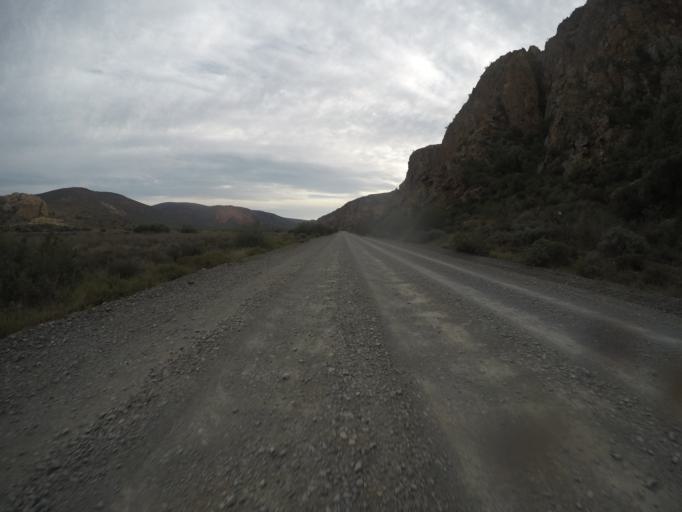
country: ZA
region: Eastern Cape
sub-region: Cacadu District Municipality
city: Willowmore
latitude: -33.5200
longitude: 23.6680
